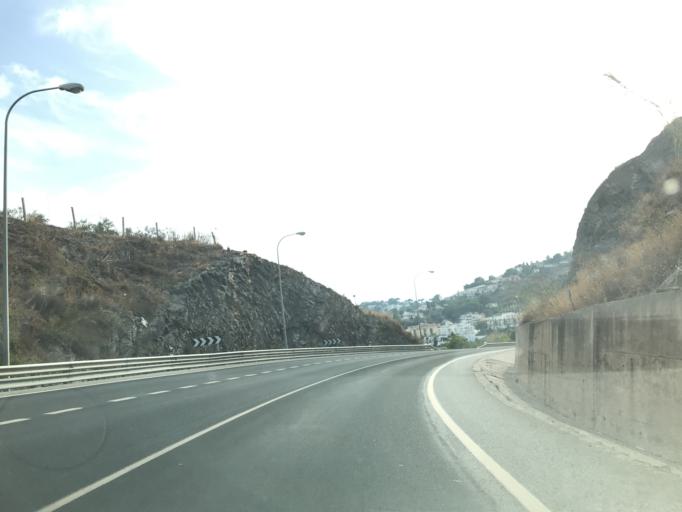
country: ES
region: Andalusia
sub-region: Provincia de Granada
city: Almunecar
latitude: 36.7503
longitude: -3.6584
